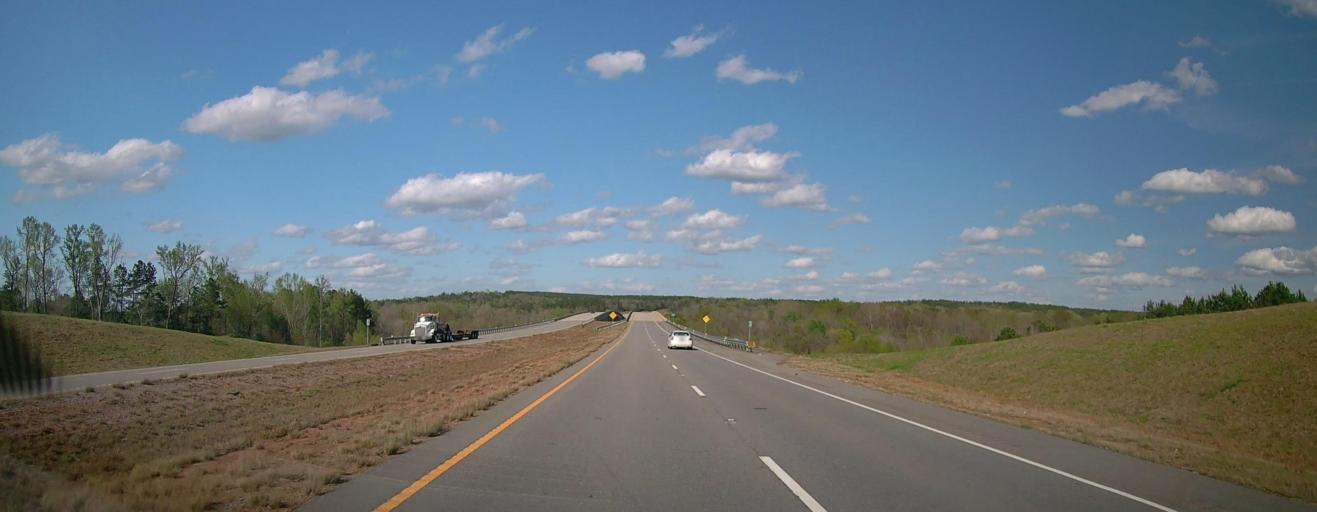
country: US
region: Georgia
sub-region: Baldwin County
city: Hardwick
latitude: 33.0210
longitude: -83.1886
